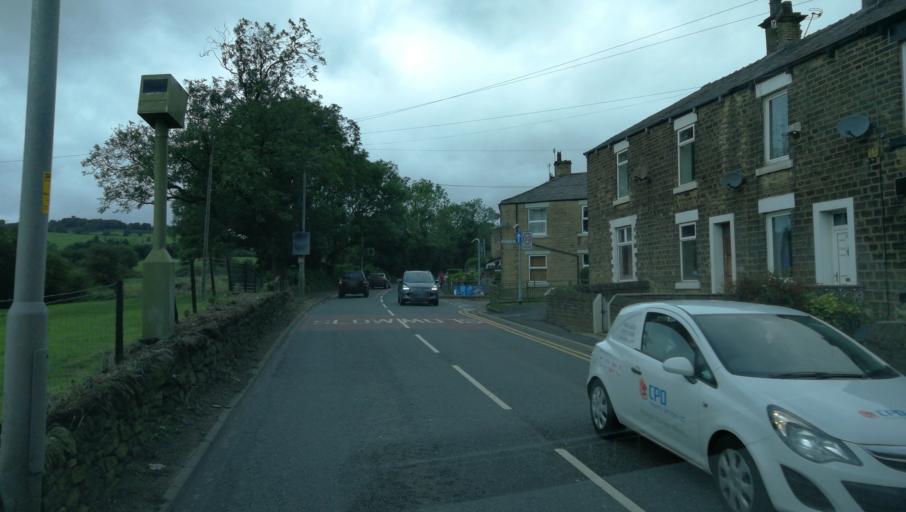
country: GB
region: England
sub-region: Borough of Tameside
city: Longdendale
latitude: 53.4587
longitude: -1.9897
